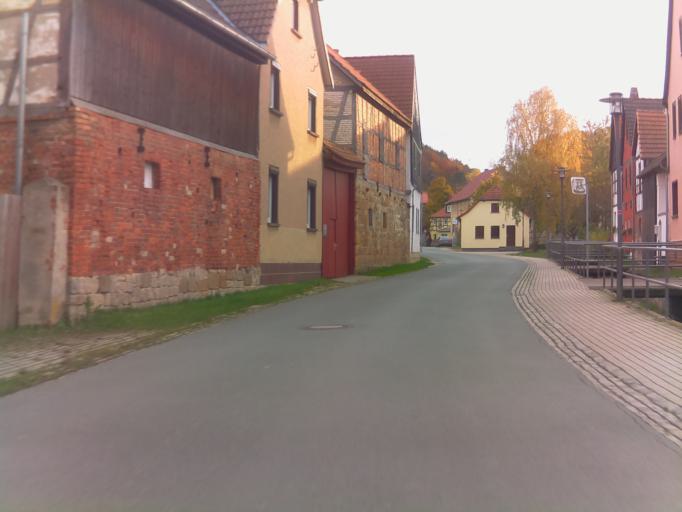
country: DE
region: Thuringia
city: Blankenhain
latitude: 50.8535
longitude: 11.3620
